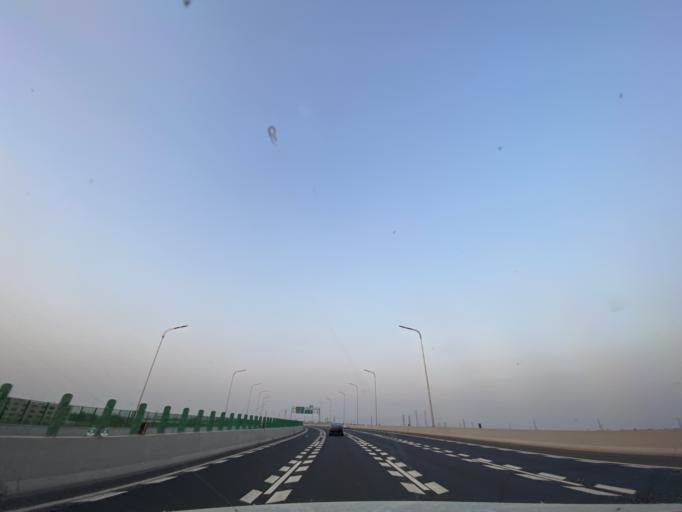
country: CN
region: Beijing
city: Xingfeng
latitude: 39.6942
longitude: 116.3745
